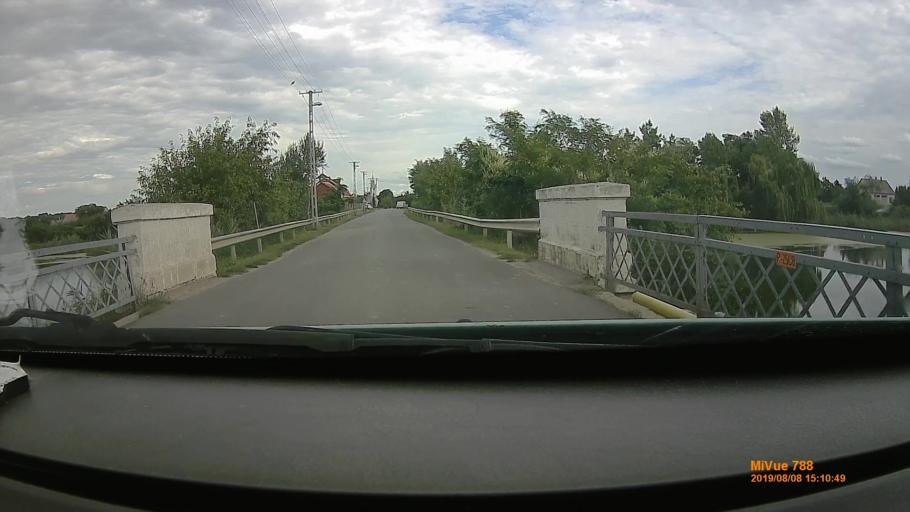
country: HU
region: Szabolcs-Szatmar-Bereg
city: Tunyogmatolcs
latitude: 47.9713
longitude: 22.4550
